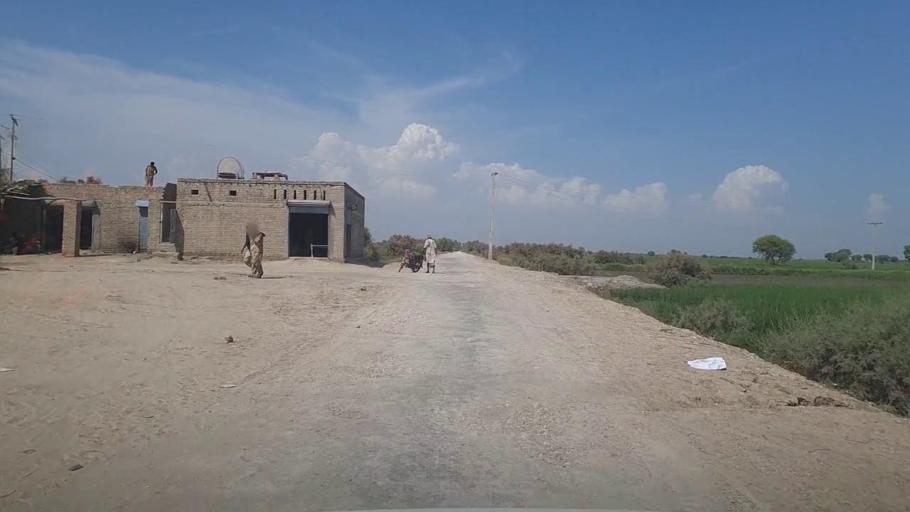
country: PK
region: Sindh
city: Kandhkot
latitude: 28.3106
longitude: 69.2009
